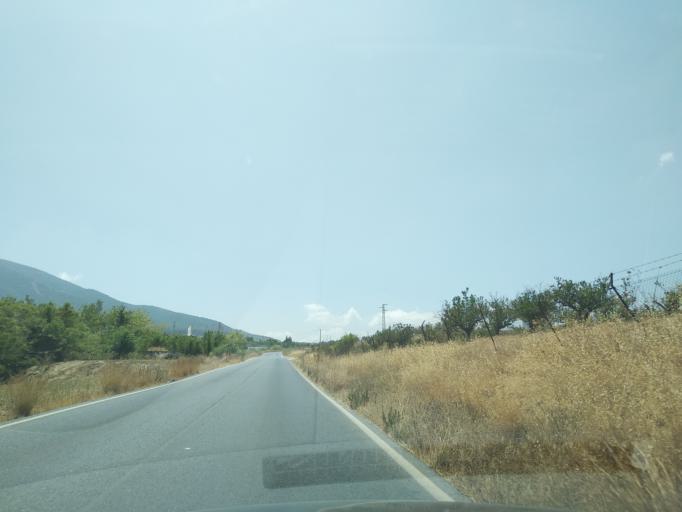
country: ES
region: Andalusia
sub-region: Provincia de Malaga
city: Alhaurin el Grande
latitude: 36.6651
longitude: -4.6691
